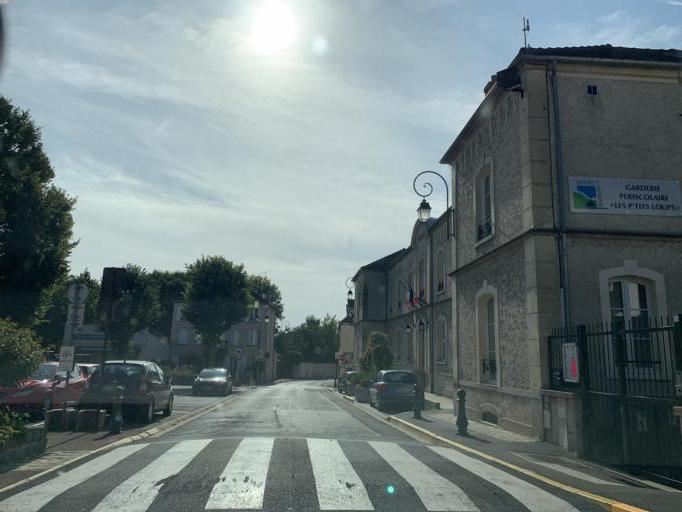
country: FR
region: Ile-de-France
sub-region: Departement de Seine-et-Marne
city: Annet-sur-Marne
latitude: 48.9258
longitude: 2.7208
